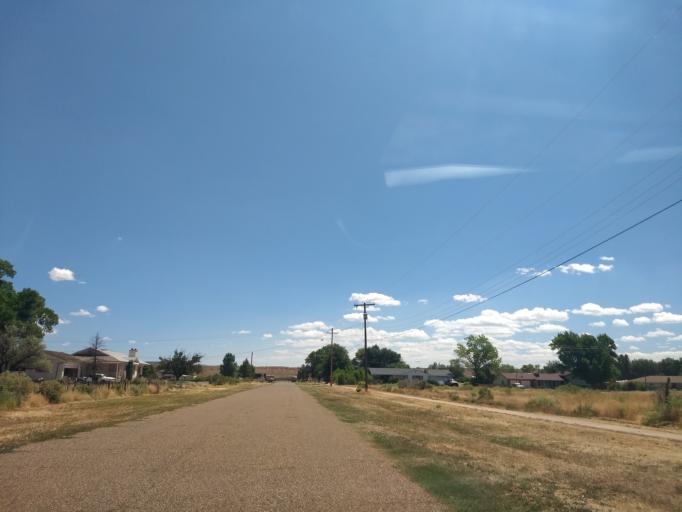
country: US
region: Arizona
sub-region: Coconino County
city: Fredonia
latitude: 36.9525
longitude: -112.5257
